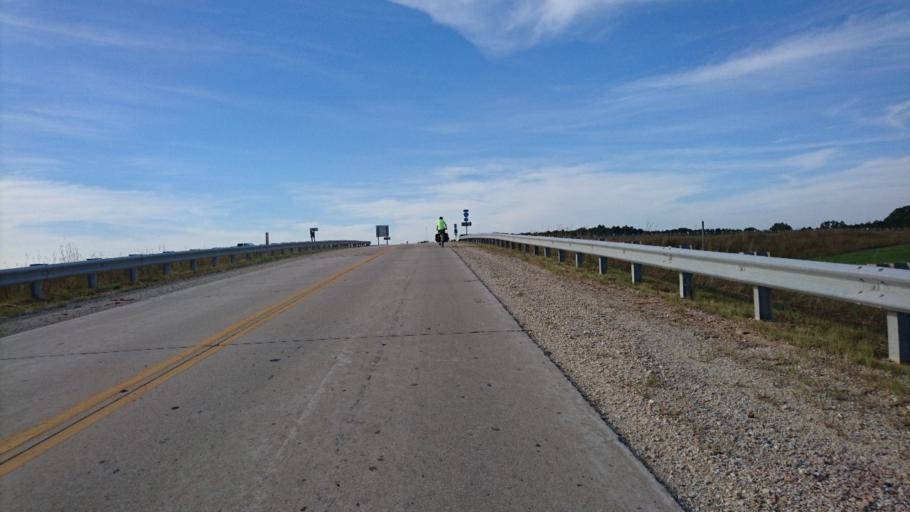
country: US
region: Missouri
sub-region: Crawford County
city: Cuba
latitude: 38.0924
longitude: -91.3674
